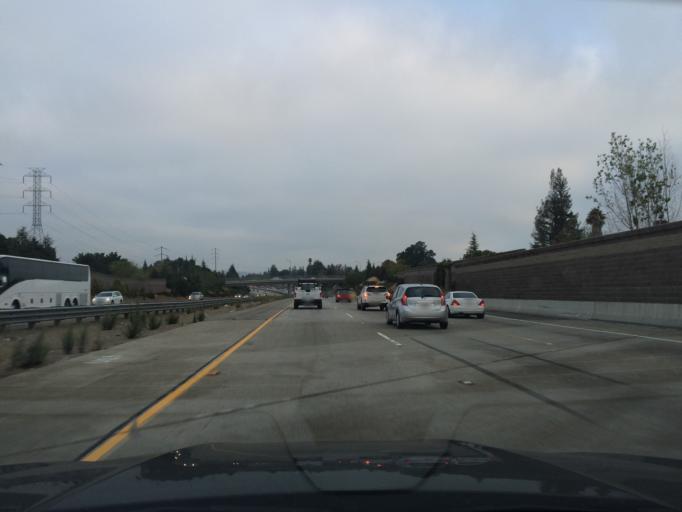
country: US
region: California
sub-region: Santa Clara County
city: Saratoga
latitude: 37.2698
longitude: -121.9906
